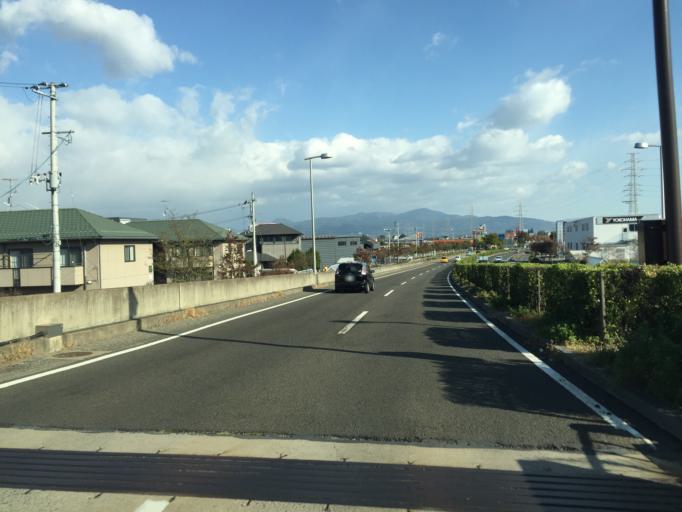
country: JP
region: Fukushima
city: Fukushima-shi
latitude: 37.7666
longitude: 140.4365
